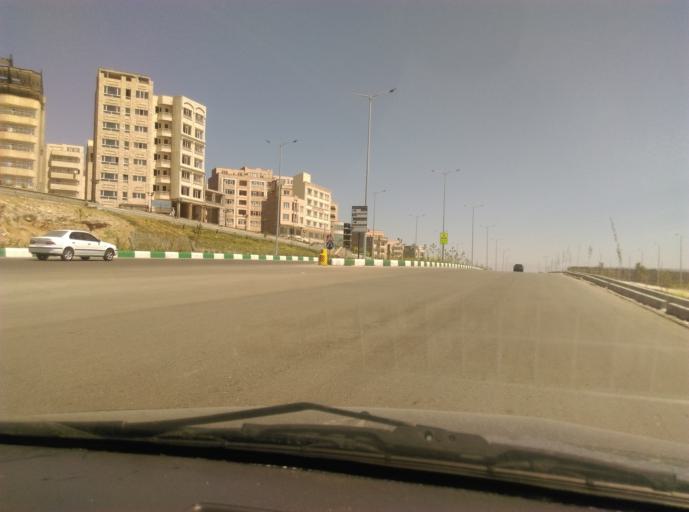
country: IR
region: Ardabil
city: Ardabil
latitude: 38.2138
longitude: 48.2698
